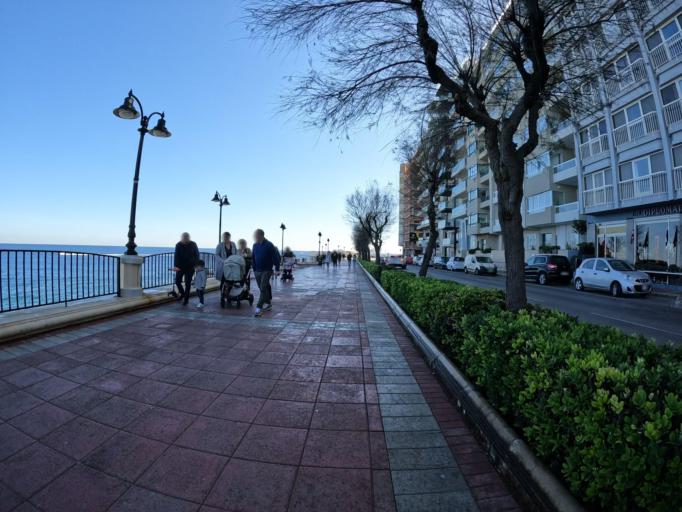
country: MT
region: Tas-Sliema
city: Sliema
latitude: 35.9166
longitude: 14.5025
